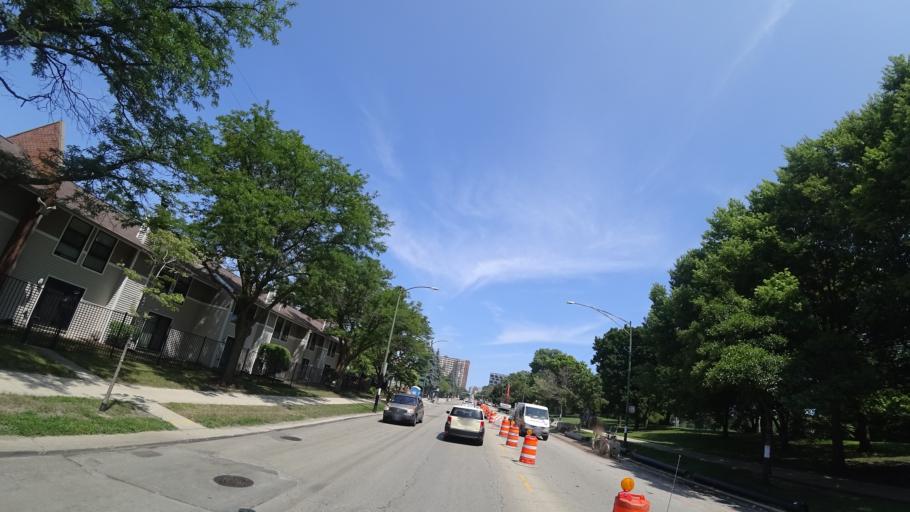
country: US
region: Illinois
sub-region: Cook County
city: Chicago
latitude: 41.7833
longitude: -87.5866
